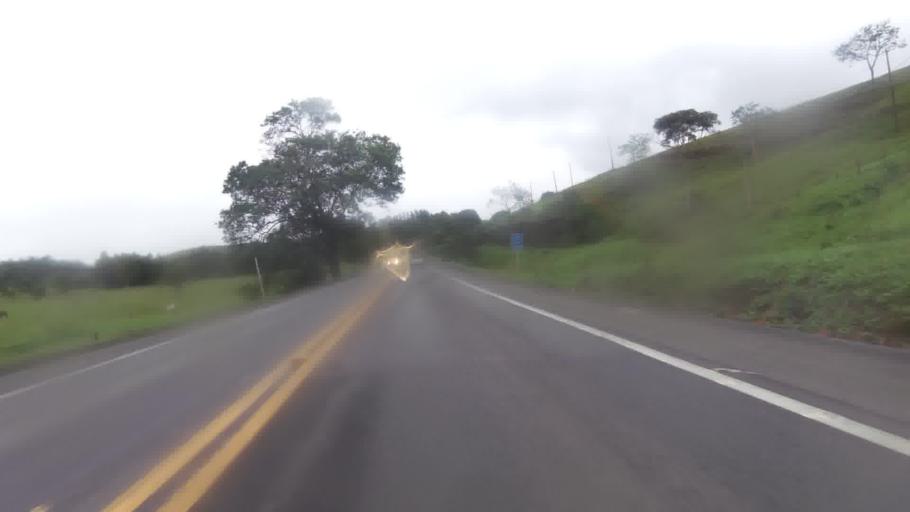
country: BR
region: Espirito Santo
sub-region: Iconha
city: Iconha
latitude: -20.7593
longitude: -40.7573
